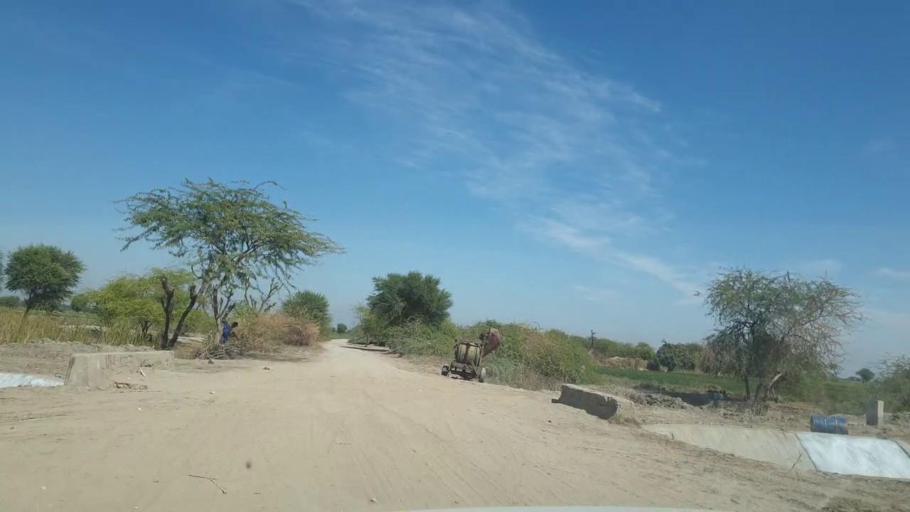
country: PK
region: Sindh
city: Pithoro
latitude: 25.6378
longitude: 69.2244
